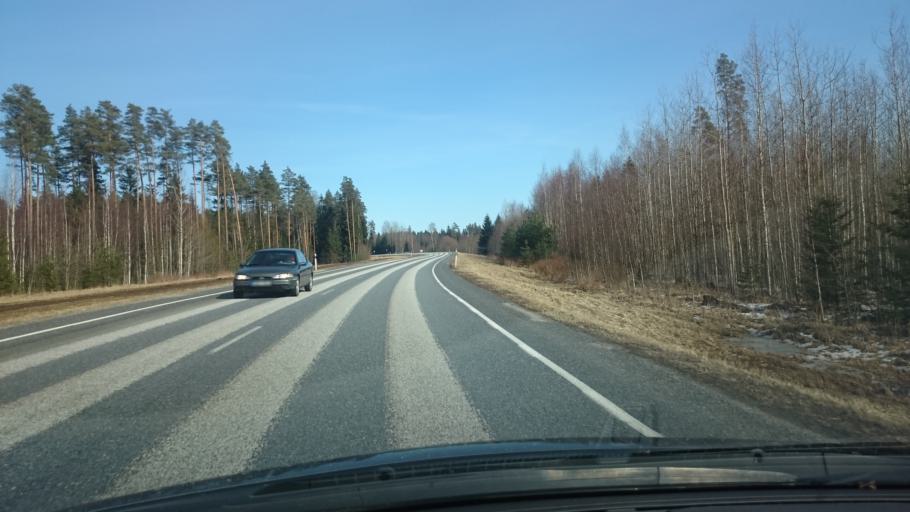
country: EE
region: Jaervamaa
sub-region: Tueri vald
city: Sarevere
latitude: 58.7329
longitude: 25.2912
